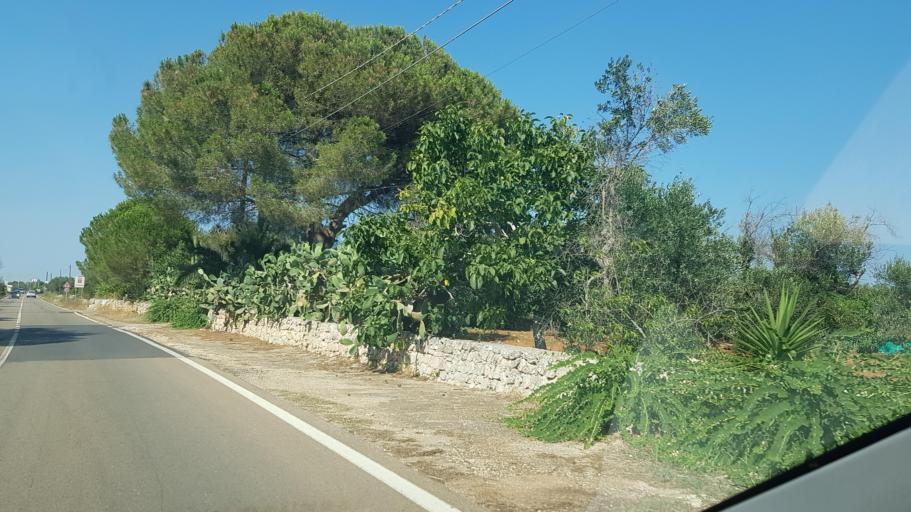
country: IT
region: Apulia
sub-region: Provincia di Lecce
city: Gemini
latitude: 39.8614
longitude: 18.2063
